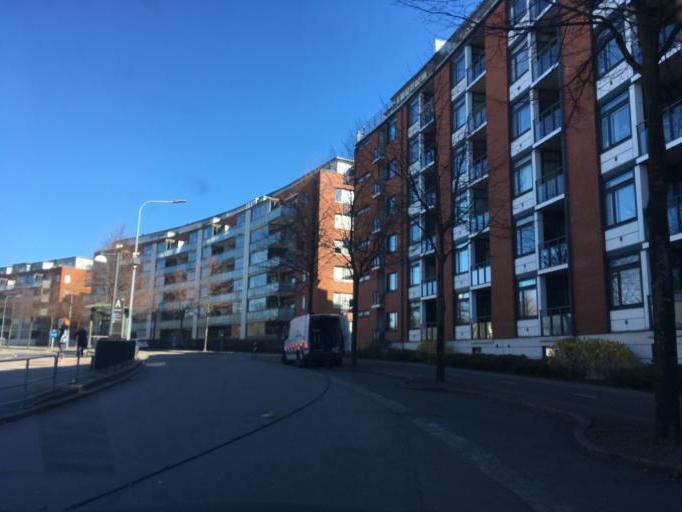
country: SE
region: Vaestra Goetaland
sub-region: Goteborg
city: Majorna
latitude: 57.7027
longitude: 11.9198
